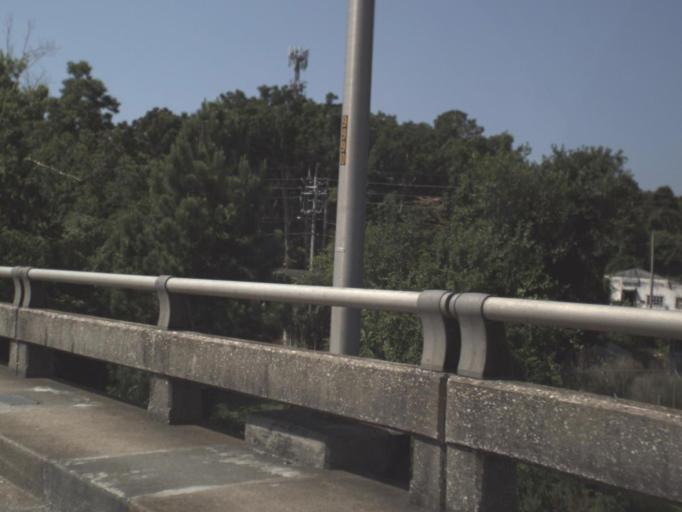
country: US
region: Florida
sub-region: Duval County
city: Jacksonville
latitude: 30.4171
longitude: -81.6966
